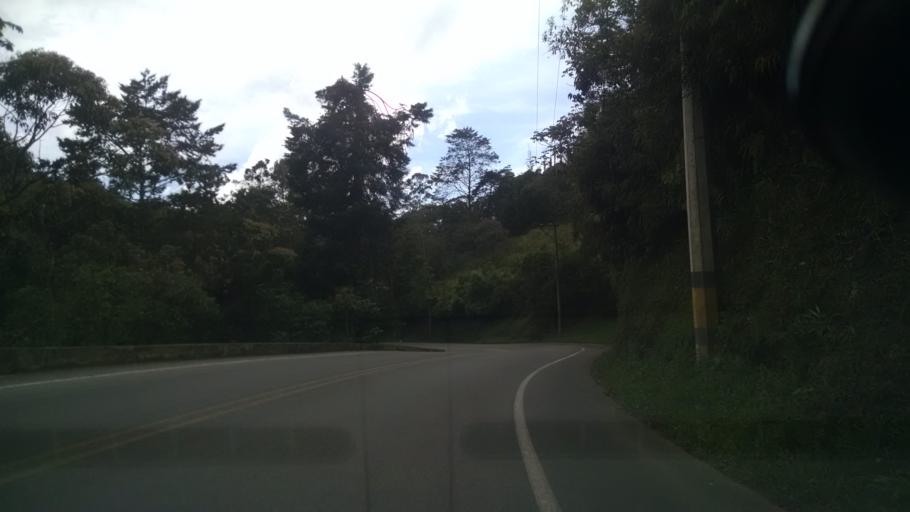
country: CO
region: Antioquia
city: Caldas
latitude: 6.0509
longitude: -75.6291
